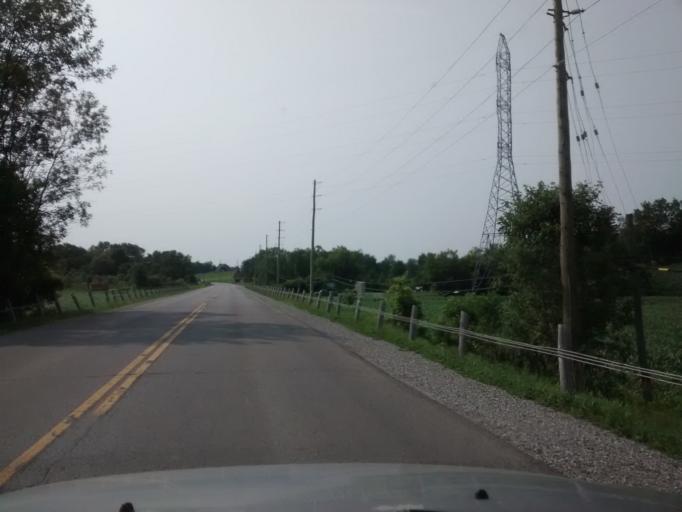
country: CA
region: Ontario
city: Ancaster
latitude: 43.0610
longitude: -79.9191
